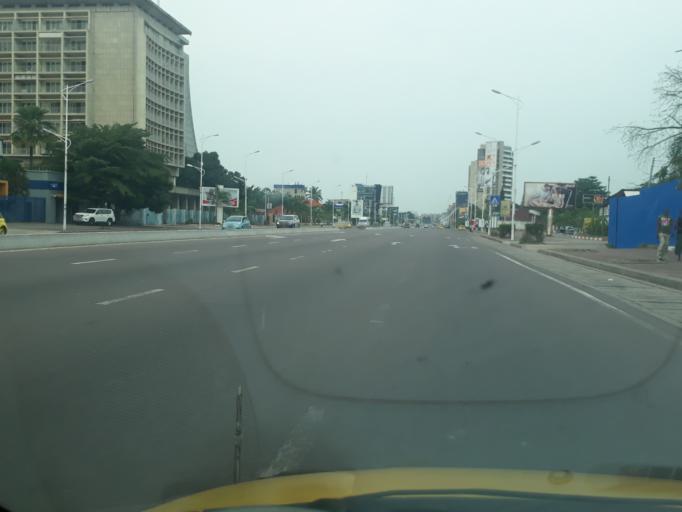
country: CD
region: Kinshasa
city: Kinshasa
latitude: -4.3152
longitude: 15.2818
